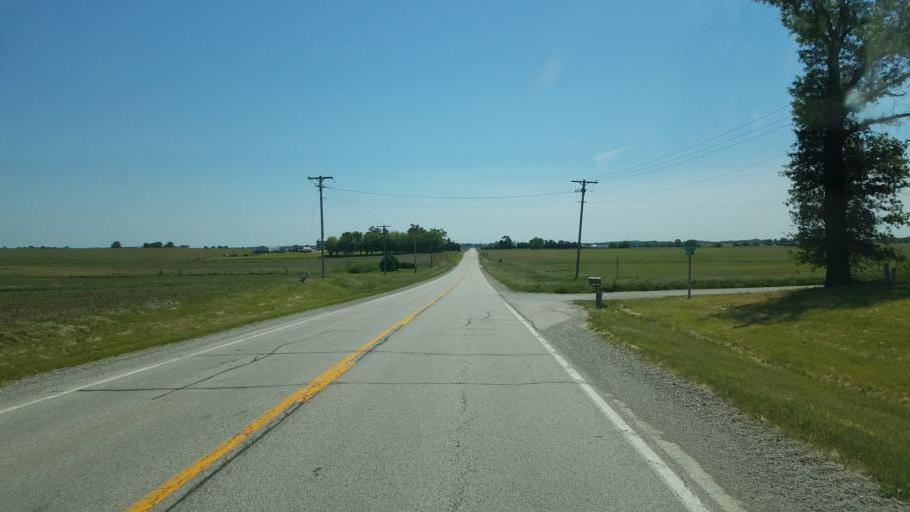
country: US
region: Illinois
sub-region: McLean County
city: Heyworth
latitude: 40.3120
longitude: -89.0704
